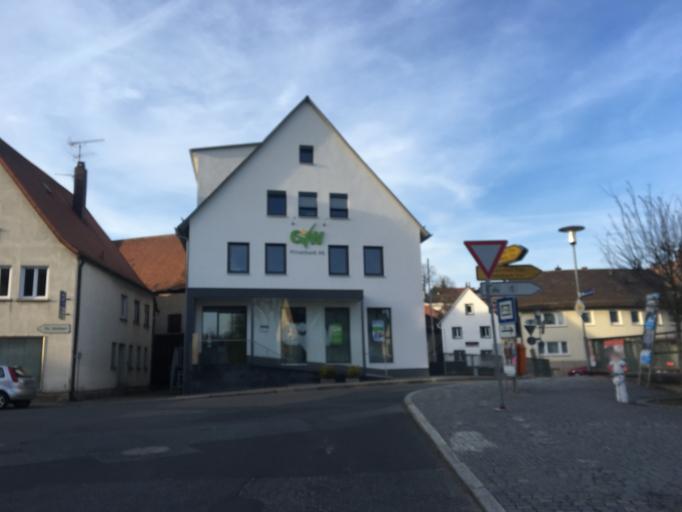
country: DE
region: Bavaria
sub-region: Regierungsbezirk Mittelfranken
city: Wilhermsdorf
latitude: 49.4820
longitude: 10.7174
